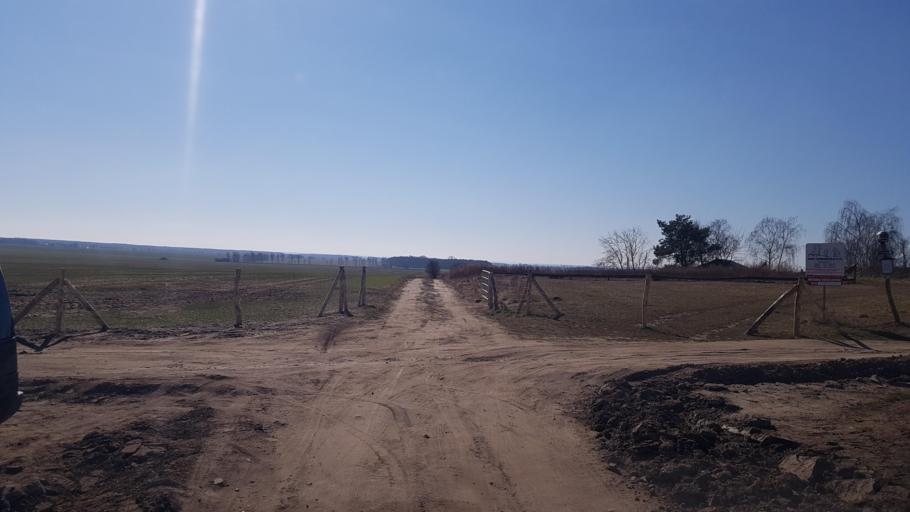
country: DE
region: Brandenburg
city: Hirschfeld
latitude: 51.3738
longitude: 13.6115
